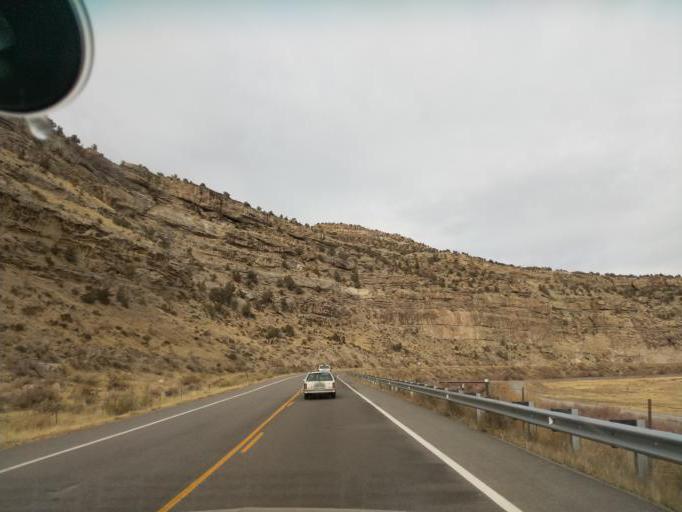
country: US
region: Colorado
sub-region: Mesa County
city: Palisade
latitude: 39.1932
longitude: -108.2296
